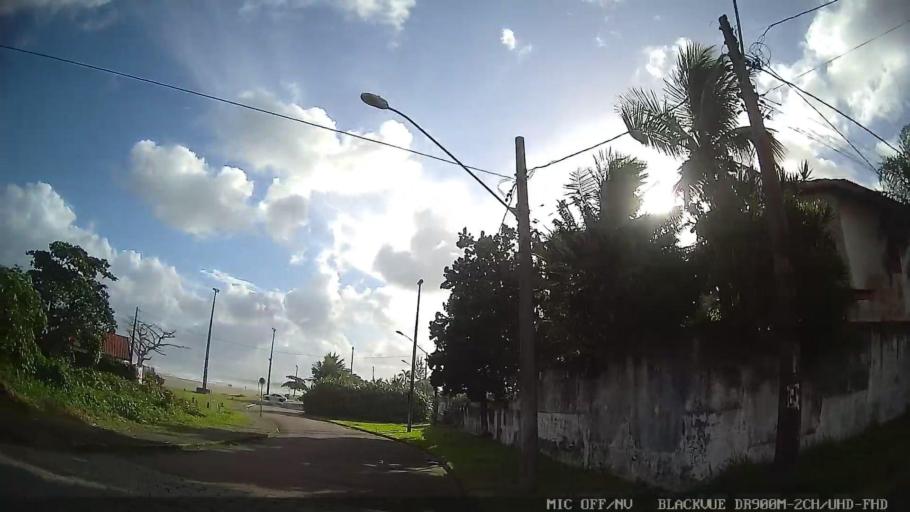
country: BR
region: Sao Paulo
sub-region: Itanhaem
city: Itanhaem
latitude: -24.1999
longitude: -46.8098
